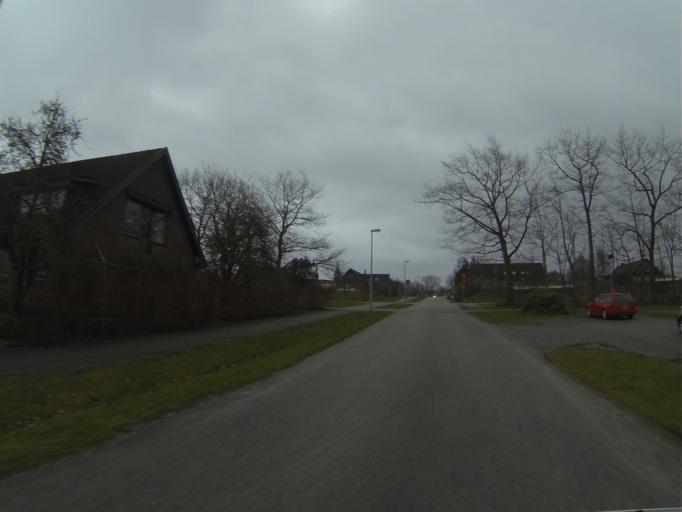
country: SE
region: Skane
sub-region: Lunds Kommun
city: Genarp
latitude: 55.7119
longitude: 13.3321
